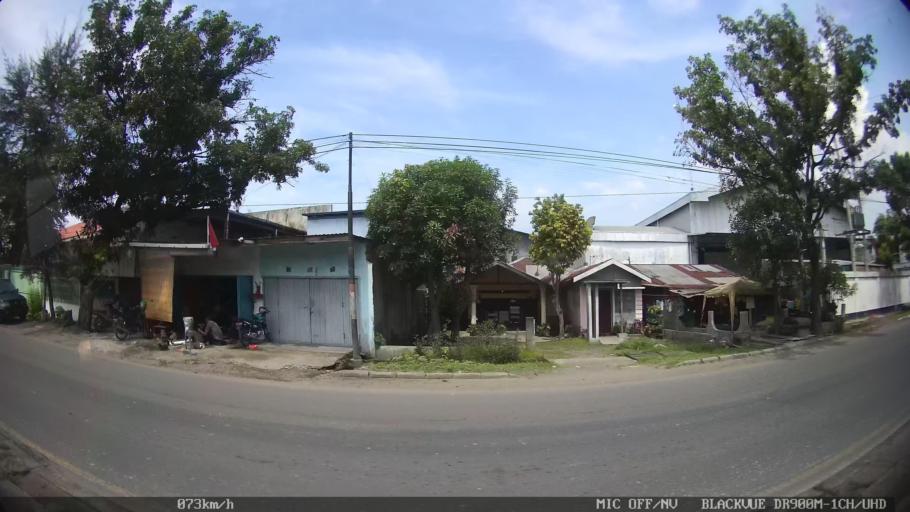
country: ID
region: North Sumatra
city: Labuhan Deli
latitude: 3.6696
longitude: 98.6673
